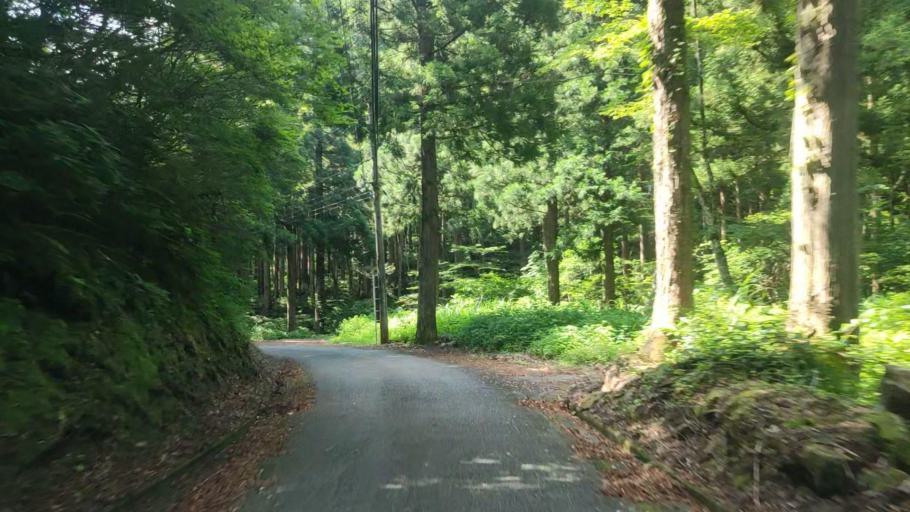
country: JP
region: Ishikawa
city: Komatsu
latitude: 36.2558
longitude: 136.5379
